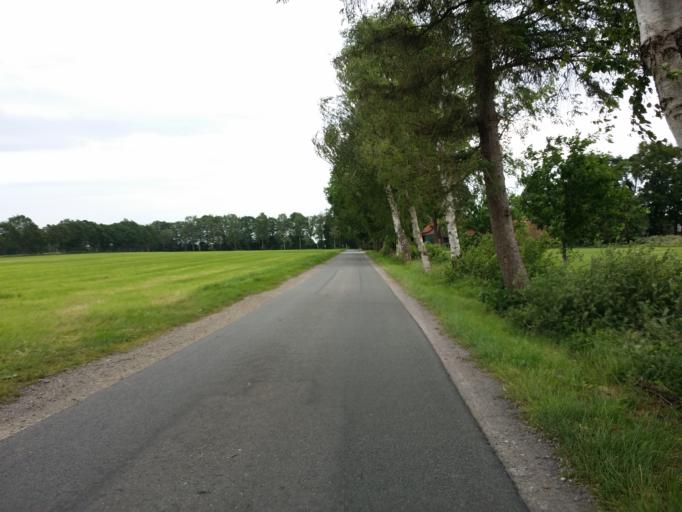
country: DE
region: Lower Saxony
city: Bockhorn
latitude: 53.3191
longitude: 8.0430
